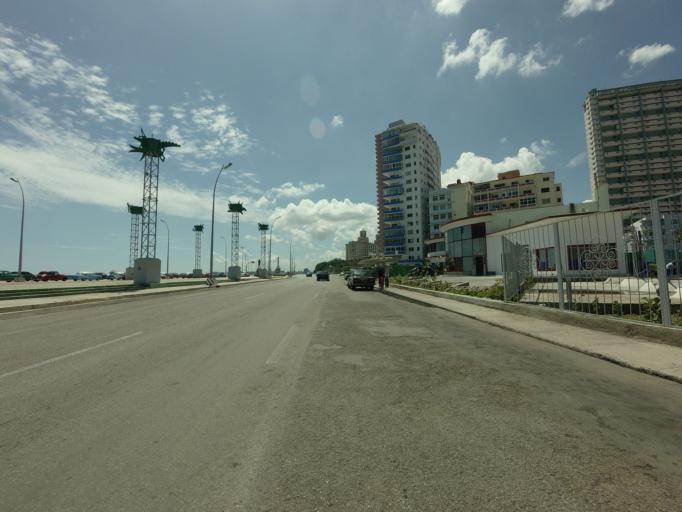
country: CU
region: La Habana
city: Havana
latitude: 23.1451
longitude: -82.3851
